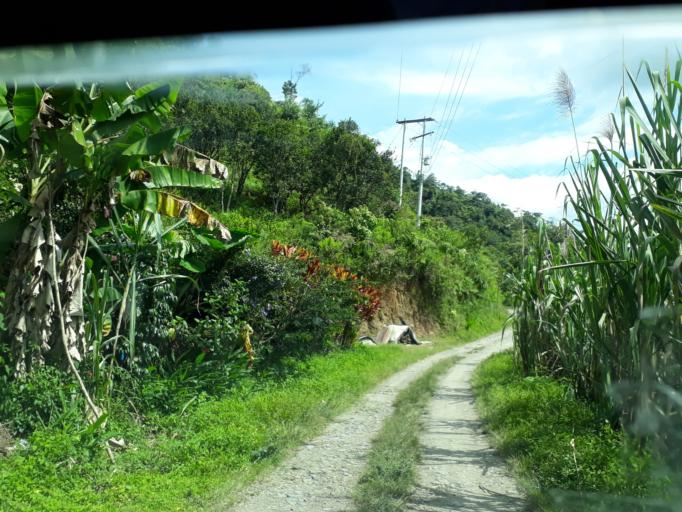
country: CO
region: Cundinamarca
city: Topaipi
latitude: 5.2880
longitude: -74.3483
